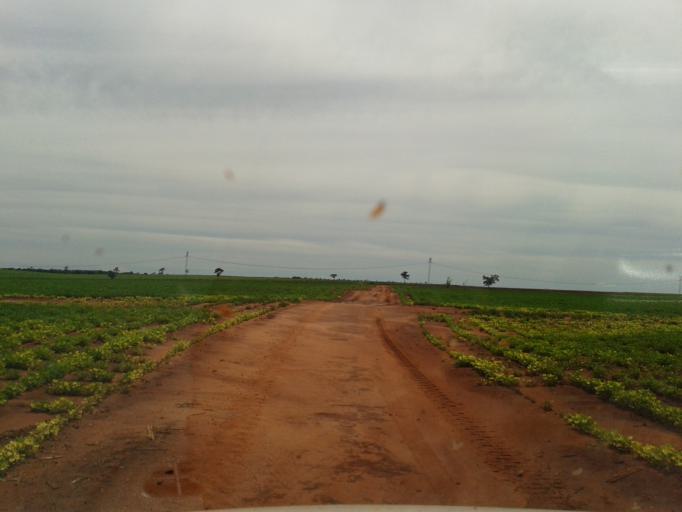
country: BR
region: Minas Gerais
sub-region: Santa Vitoria
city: Santa Vitoria
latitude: -19.2084
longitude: -50.6310
